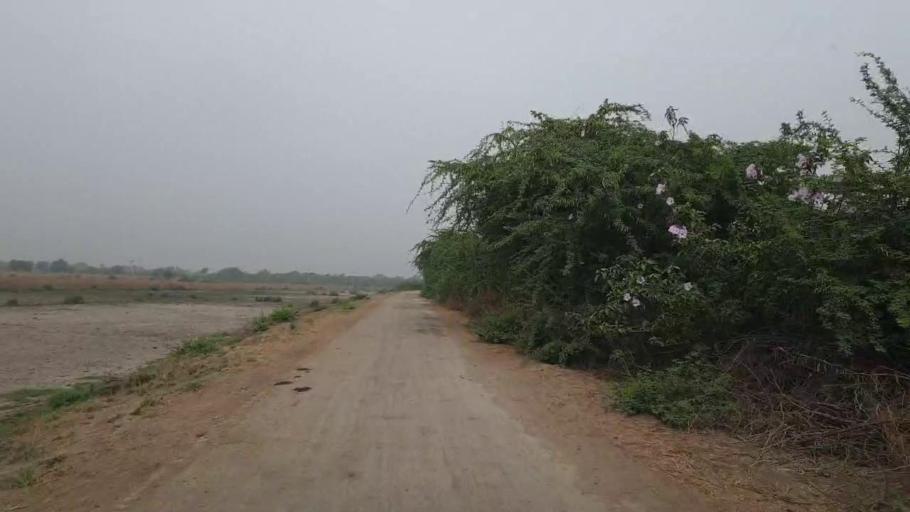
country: PK
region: Sindh
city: Badin
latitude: 24.5817
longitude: 68.6678
